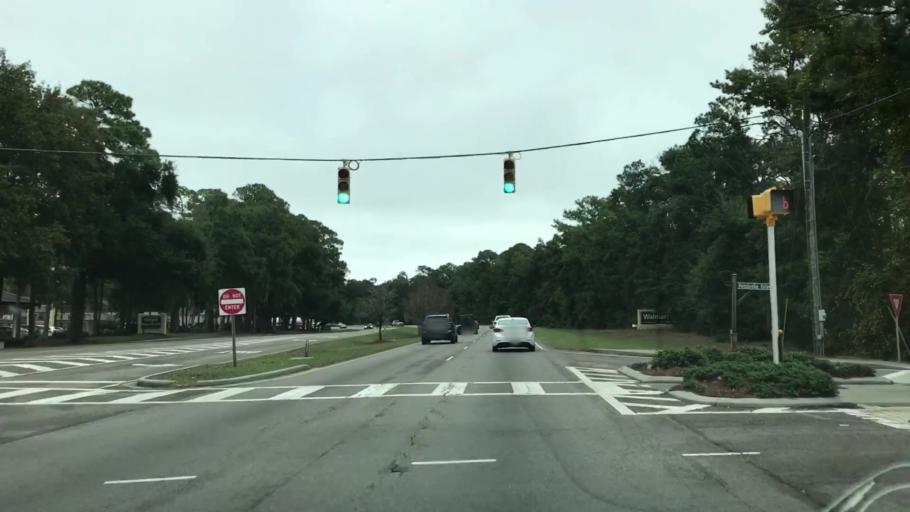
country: US
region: South Carolina
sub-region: Beaufort County
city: Hilton Head Island
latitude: 32.2131
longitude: -80.7294
